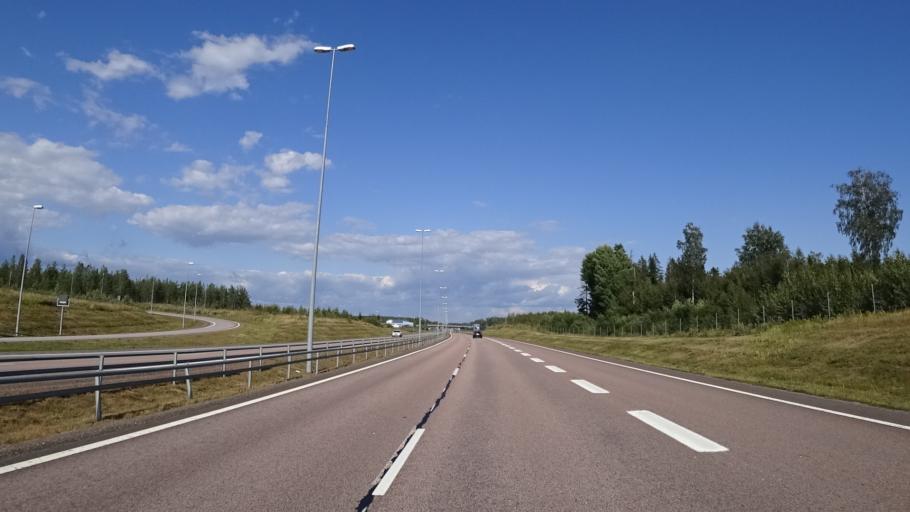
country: FI
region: Kymenlaakso
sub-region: Kotka-Hamina
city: Hamina
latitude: 60.5744
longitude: 27.1344
